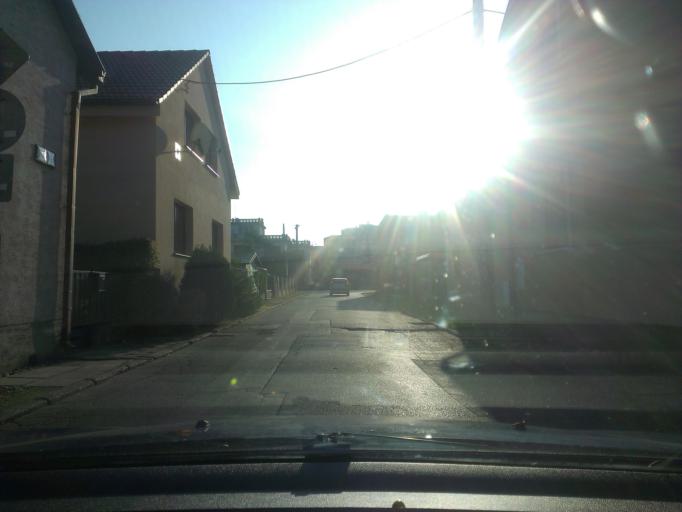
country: SK
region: Trnavsky
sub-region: Okres Trnava
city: Piestany
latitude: 48.5895
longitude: 17.8179
